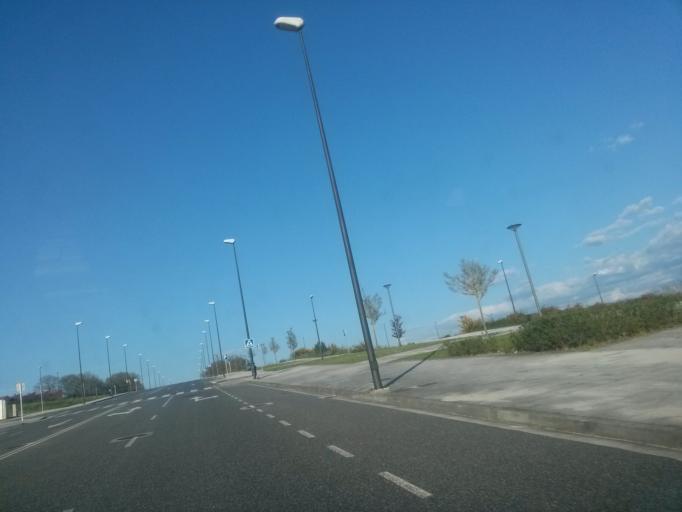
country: ES
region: Galicia
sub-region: Provincia de Lugo
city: Lugo
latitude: 42.9958
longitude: -7.5427
